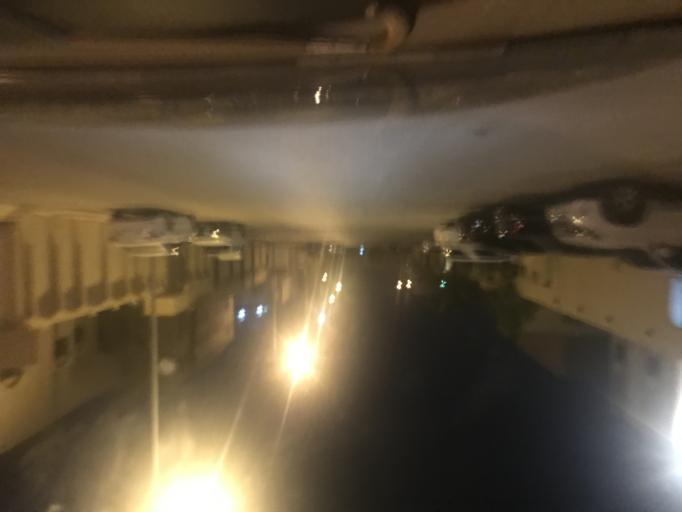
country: SA
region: Ar Riyad
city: Riyadh
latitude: 24.7577
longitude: 46.7622
